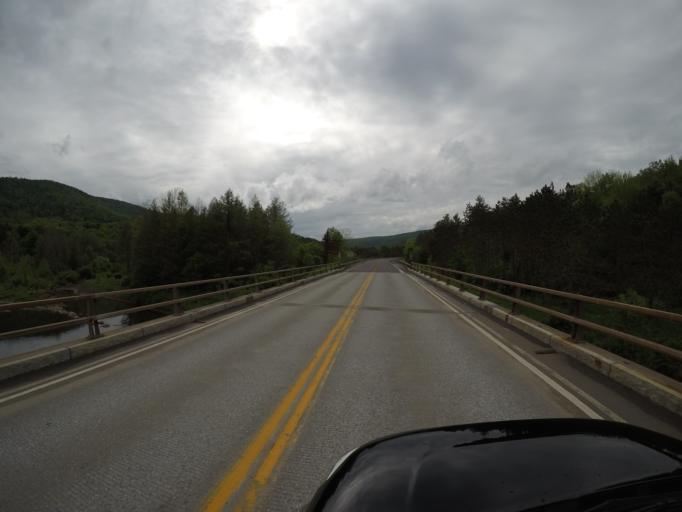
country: US
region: New York
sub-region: Sullivan County
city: Livingston Manor
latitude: 42.1217
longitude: -74.6801
